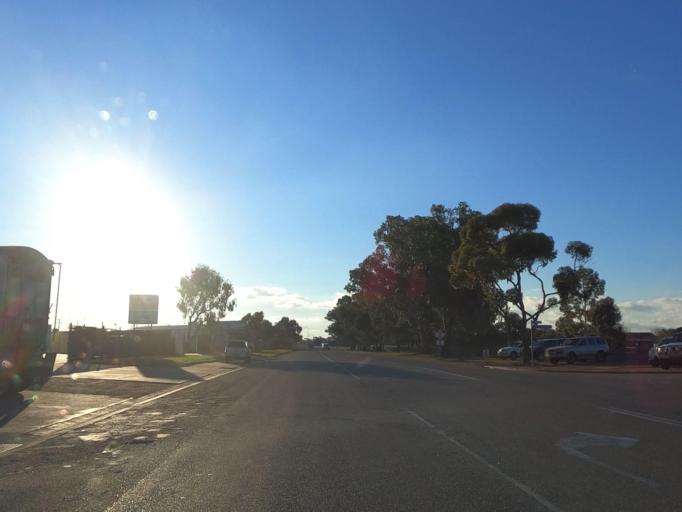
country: AU
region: Victoria
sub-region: Swan Hill
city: Swan Hill
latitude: -35.3302
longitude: 143.5562
